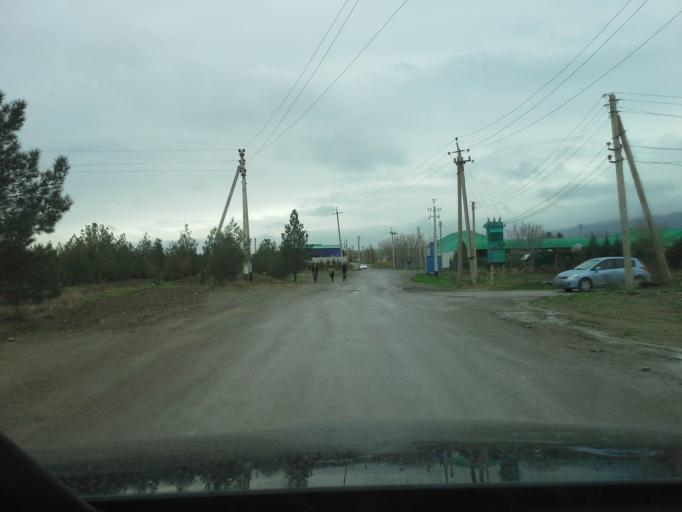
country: TM
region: Ahal
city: Abadan
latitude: 37.9663
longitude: 58.2290
